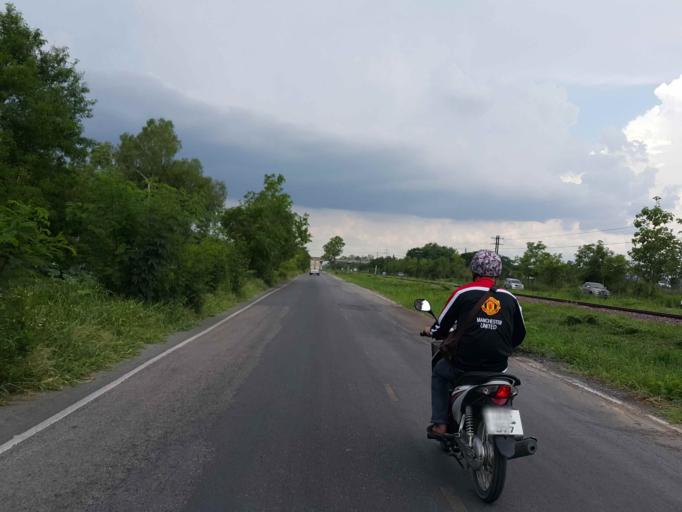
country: TH
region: Chiang Mai
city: Saraphi
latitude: 18.7382
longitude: 99.0298
